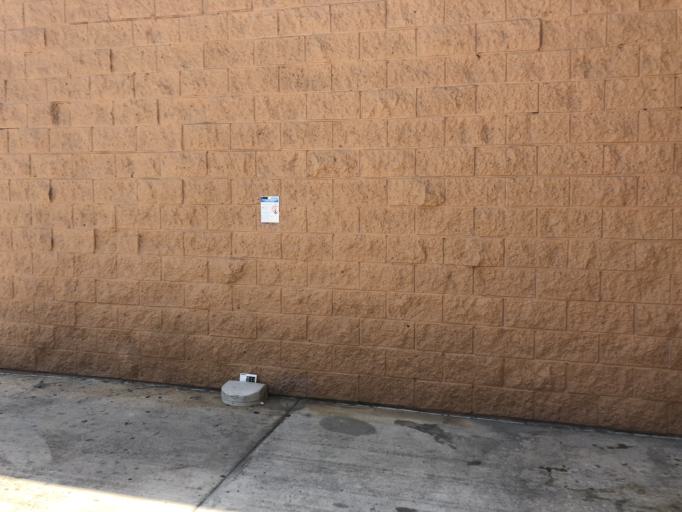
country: MX
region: Chiapas
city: Tuxtla Gutierrez
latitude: 16.7461
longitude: -93.0736
